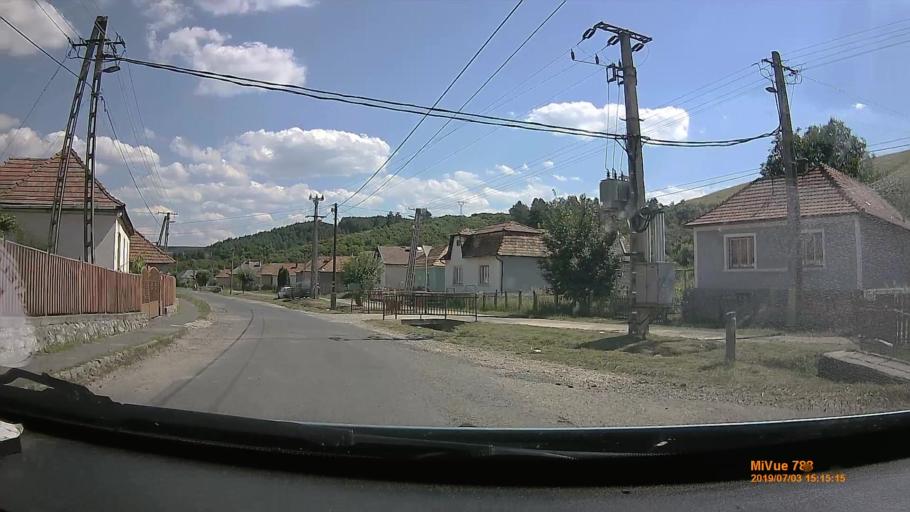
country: HU
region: Borsod-Abauj-Zemplen
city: Farkaslyuk
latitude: 48.2152
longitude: 20.3916
